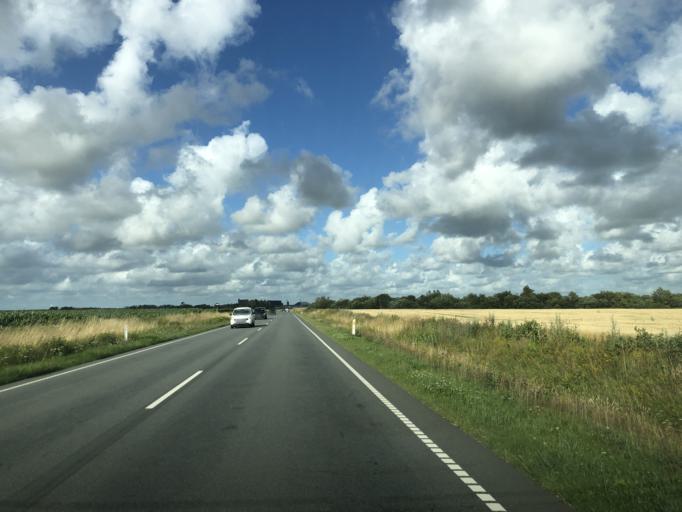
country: DK
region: Central Jutland
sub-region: Lemvig Kommune
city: Lemvig
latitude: 56.5068
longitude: 8.2859
